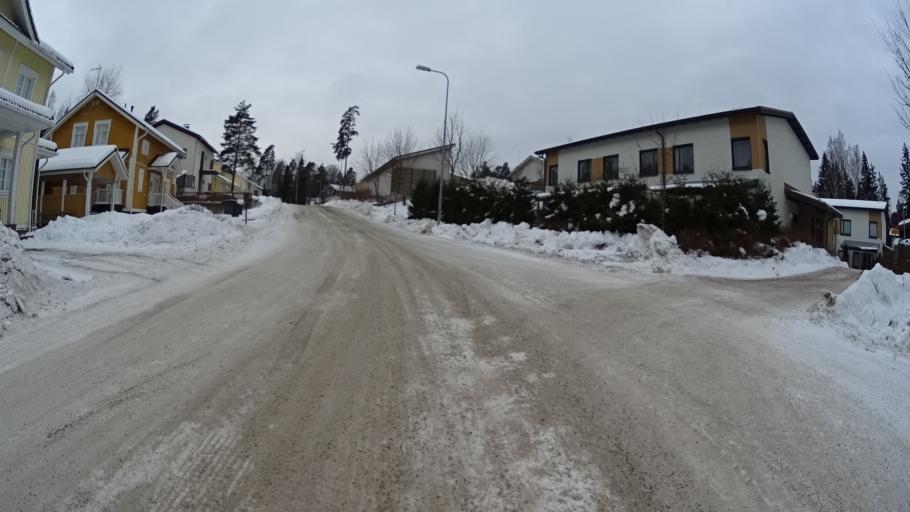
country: FI
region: Uusimaa
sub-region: Helsinki
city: Espoo
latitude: 60.2205
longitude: 24.6275
